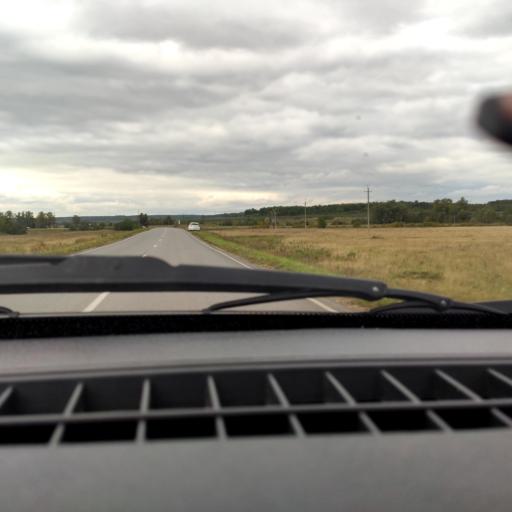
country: RU
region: Bashkortostan
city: Iglino
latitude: 54.7242
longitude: 56.4049
